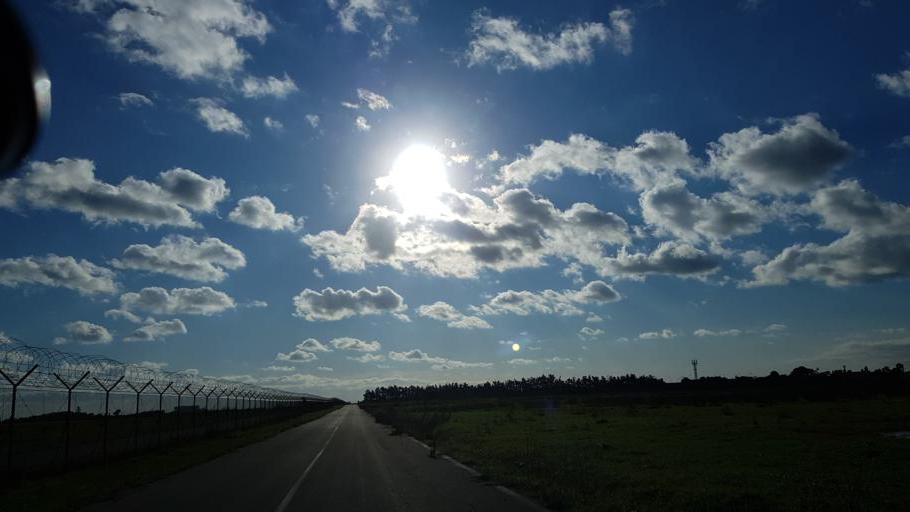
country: IT
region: Apulia
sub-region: Provincia di Brindisi
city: Materdomini
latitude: 40.6707
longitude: 17.9289
